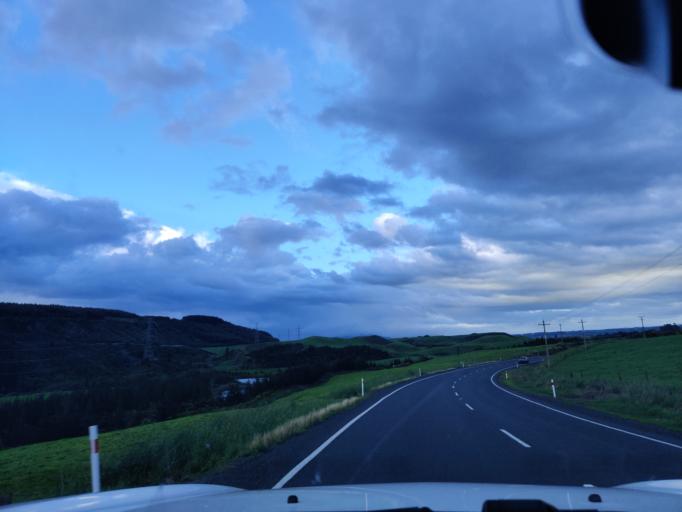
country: NZ
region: Waikato
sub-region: South Waikato District
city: Tokoroa
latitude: -38.3731
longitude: 175.8011
